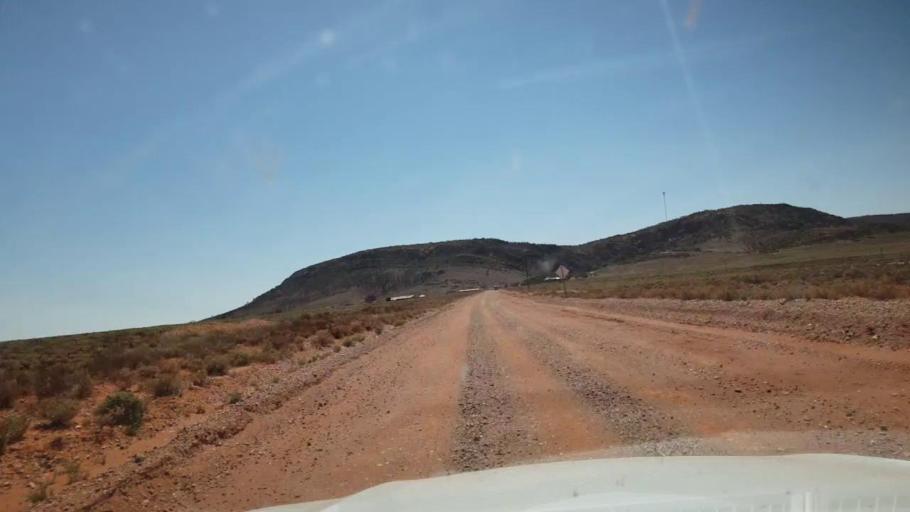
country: AU
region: South Australia
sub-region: Whyalla
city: Whyalla
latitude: -32.6920
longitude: 137.1292
